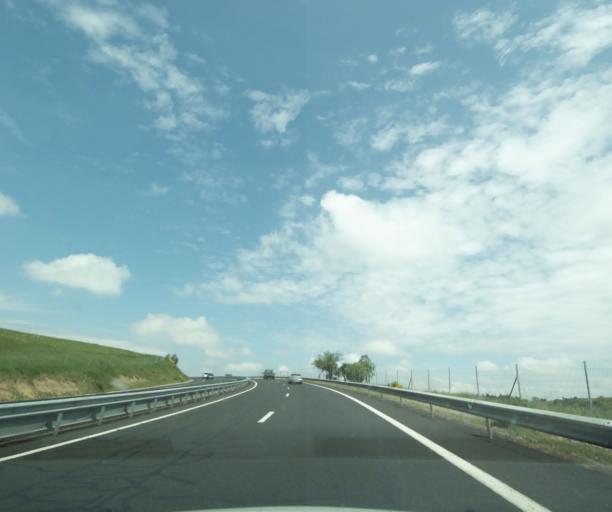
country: FR
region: Auvergne
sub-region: Departement du Cantal
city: Saint-Flour
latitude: 45.0996
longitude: 3.1290
